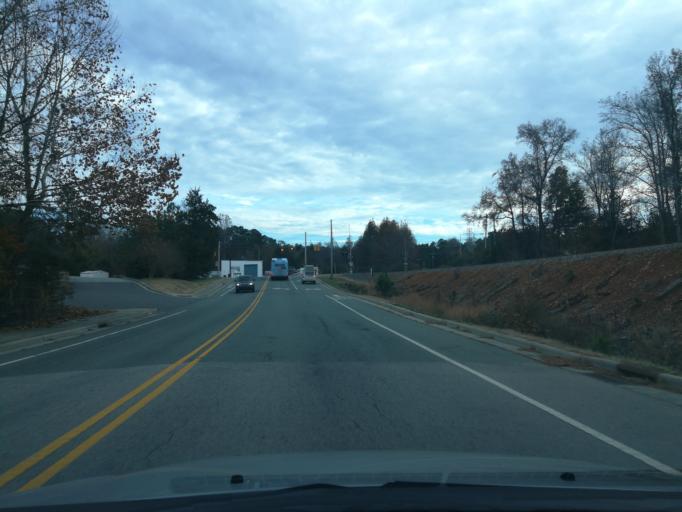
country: US
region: North Carolina
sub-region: Orange County
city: Carrboro
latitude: 35.9706
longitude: -79.0756
